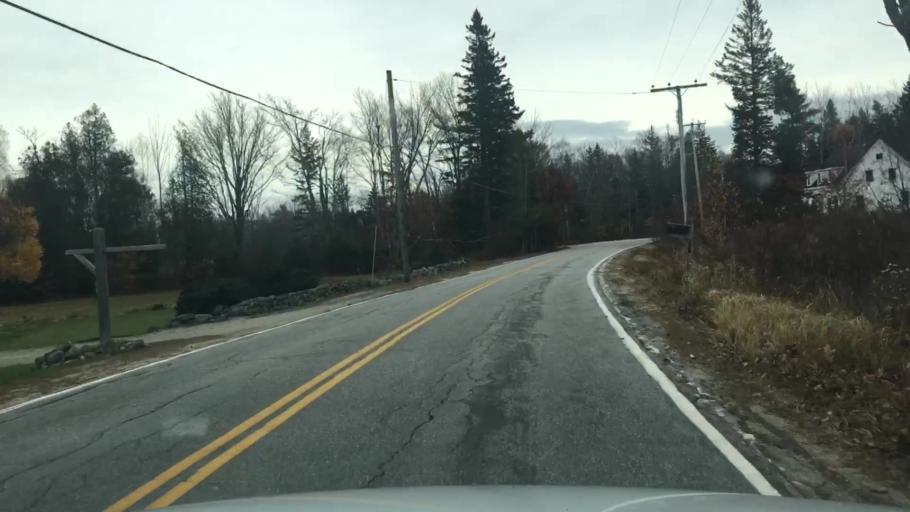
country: US
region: Maine
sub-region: Hancock County
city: Sedgwick
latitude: 44.3014
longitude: -68.5611
